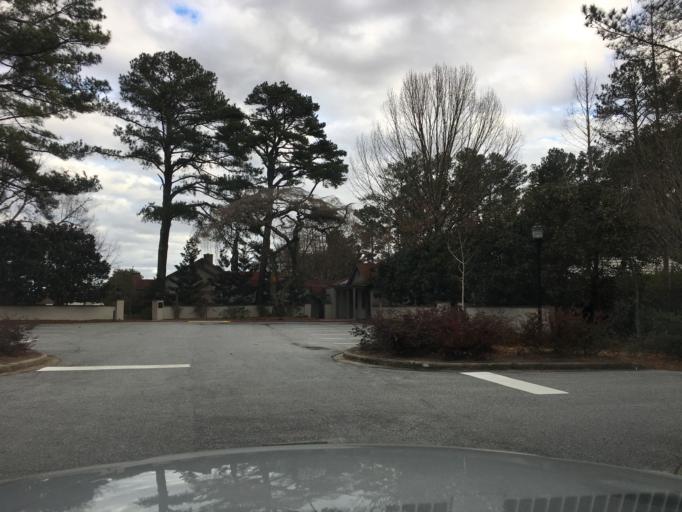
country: US
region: South Carolina
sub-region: Spartanburg County
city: Saxon
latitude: 34.9888
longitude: -81.9630
